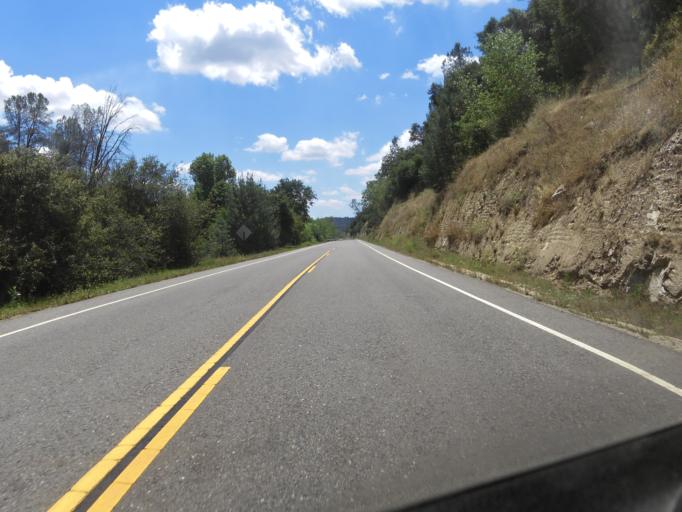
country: US
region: California
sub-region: Madera County
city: Coarsegold
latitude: 37.1775
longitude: -119.6307
